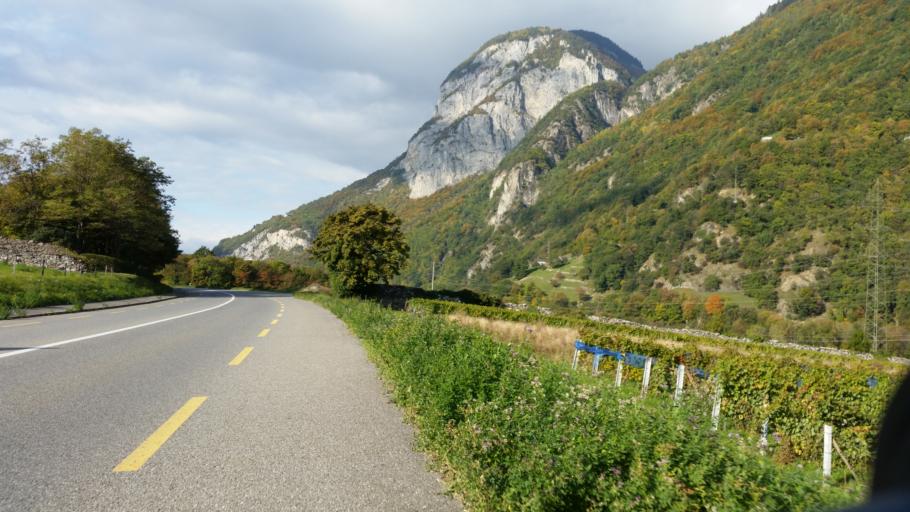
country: CH
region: Valais
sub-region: Martigny District
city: Evionnaz
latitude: 46.1873
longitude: 7.0278
